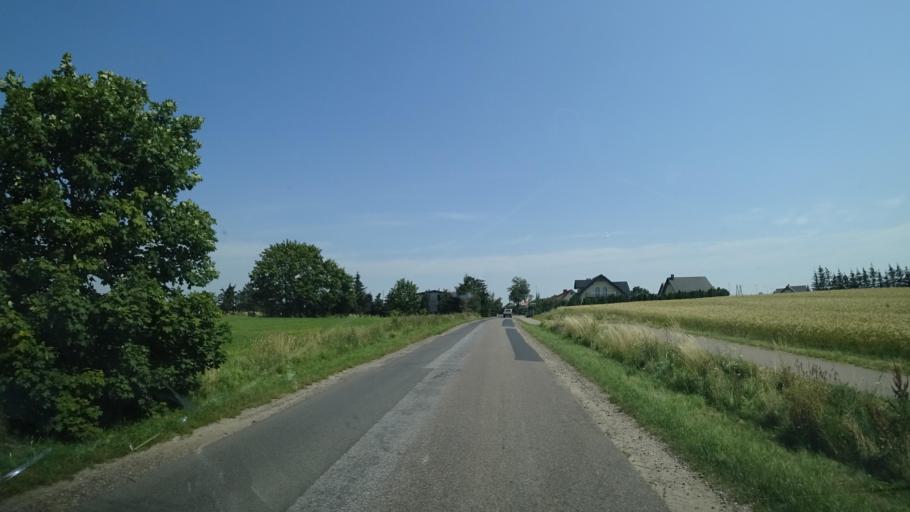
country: PL
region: Pomeranian Voivodeship
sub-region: Powiat chojnicki
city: Brusy
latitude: 53.8833
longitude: 17.7027
